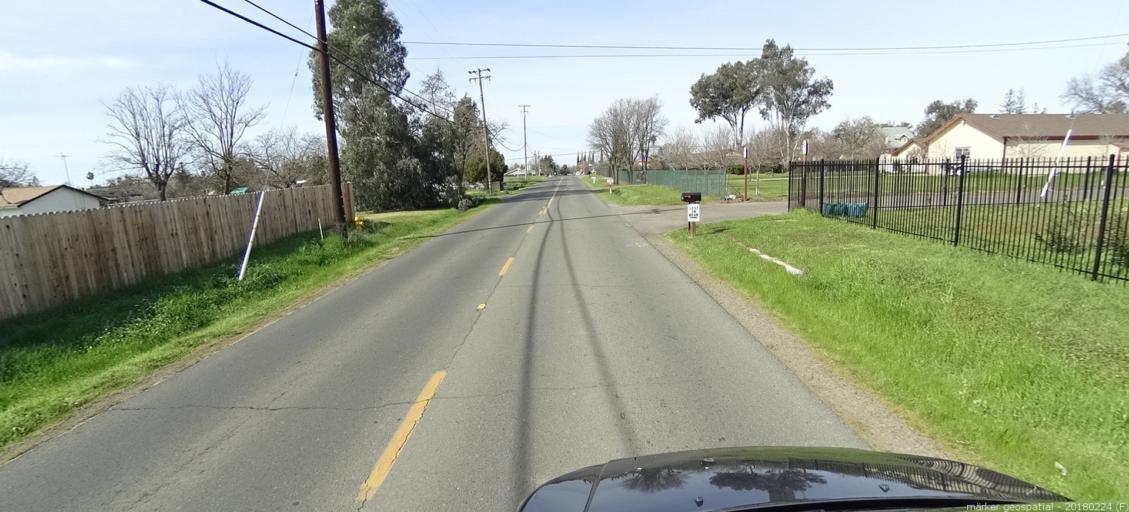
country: US
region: California
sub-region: Sacramento County
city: Rio Linda
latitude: 38.6764
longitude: -121.4365
